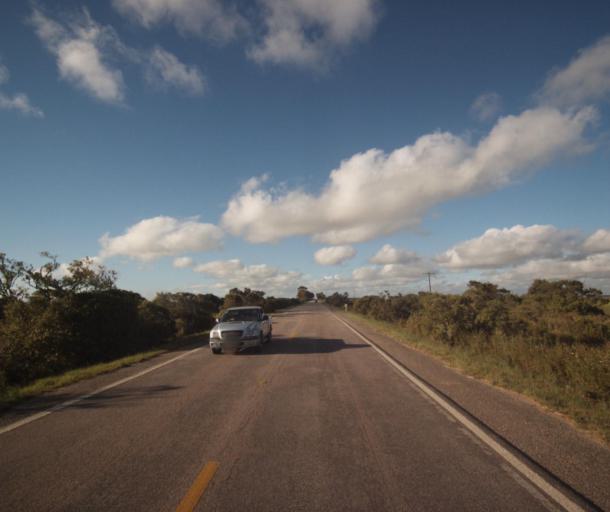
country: BR
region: Rio Grande do Sul
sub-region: Arroio Grande
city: Arroio Grande
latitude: -32.4872
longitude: -52.5795
